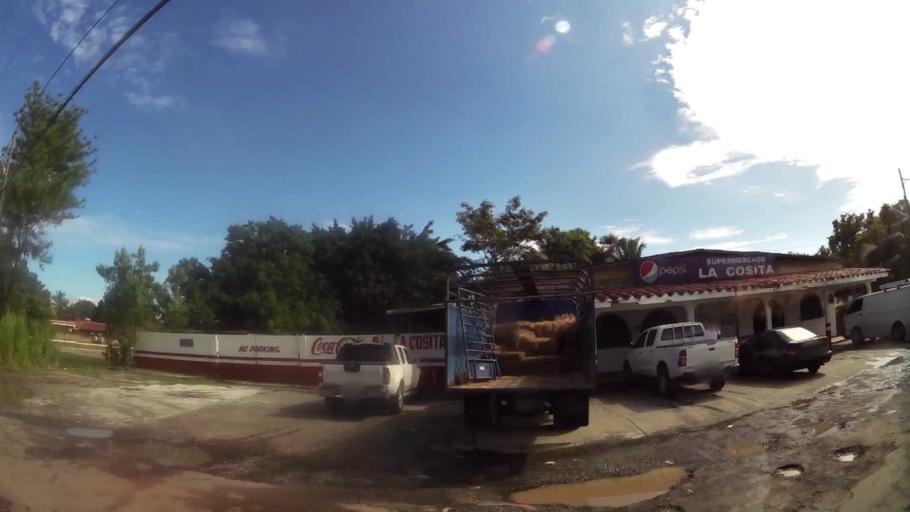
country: PA
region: Panama
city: Nueva Gorgona
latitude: 8.5280
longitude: -79.8929
